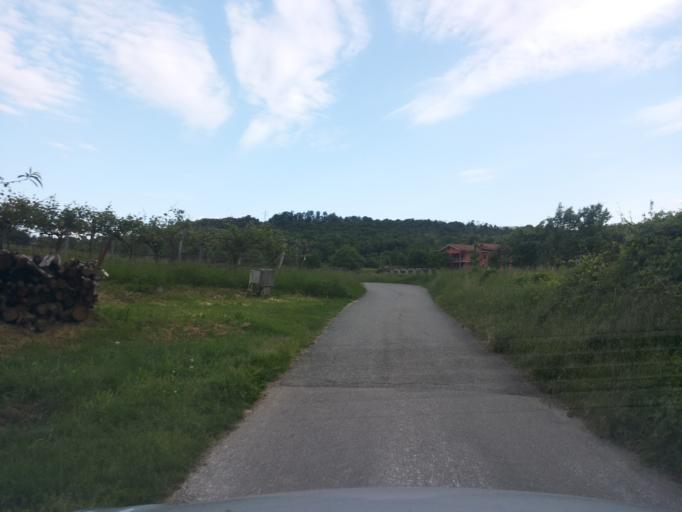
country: IT
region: Piedmont
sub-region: Provincia di Torino
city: Cossano Canavese
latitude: 45.3894
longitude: 8.0020
